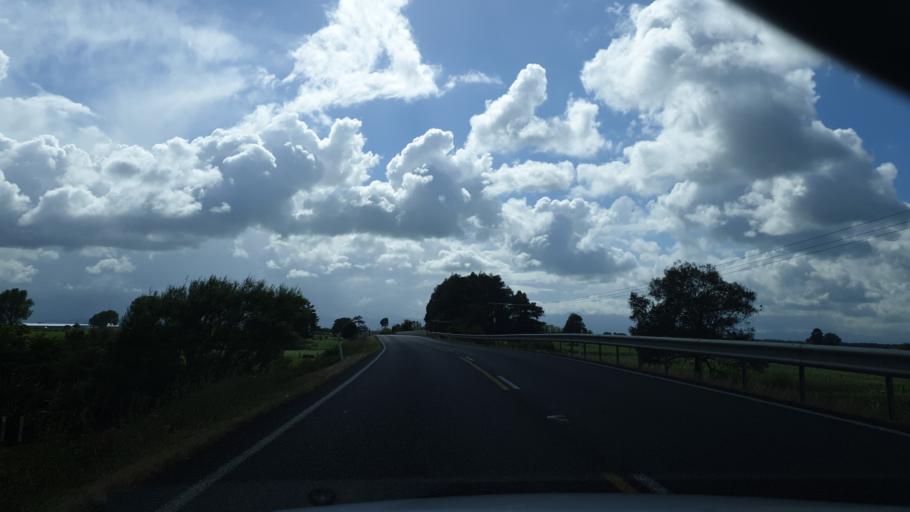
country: NZ
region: Waikato
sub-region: Hauraki District
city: Paeroa
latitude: -37.5145
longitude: 175.5044
